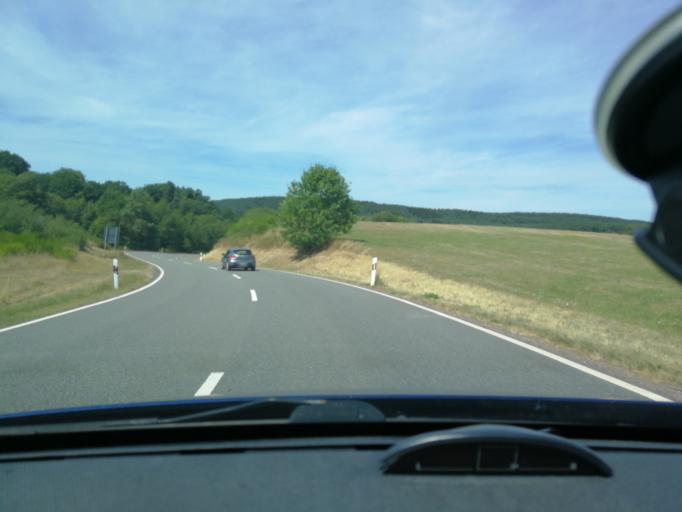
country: DE
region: Rheinland-Pfalz
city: Binsfeld
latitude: 49.9754
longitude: 6.7390
